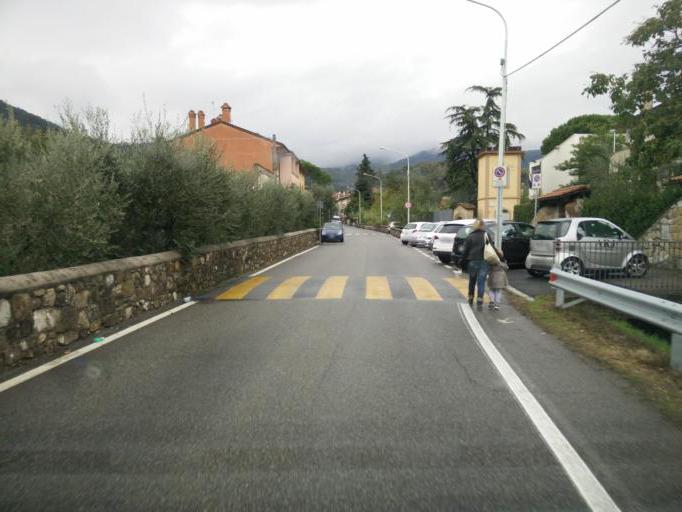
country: IT
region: Tuscany
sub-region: Provincia di Prato
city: Prato
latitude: 43.9168
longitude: 11.0951
